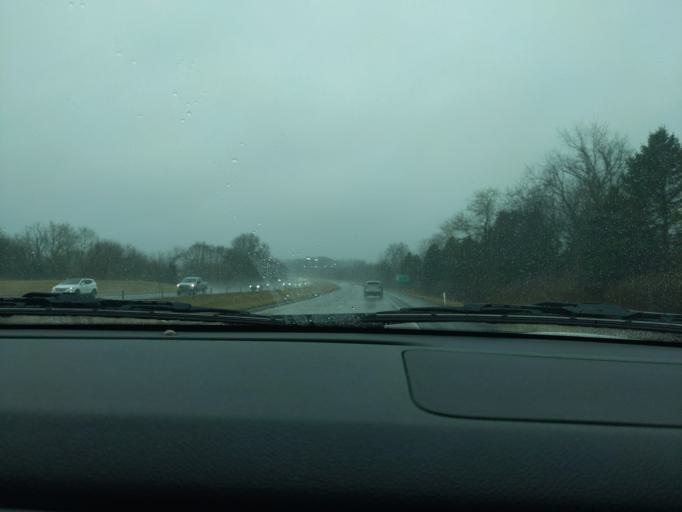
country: US
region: Pennsylvania
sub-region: Bucks County
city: Doylestown
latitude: 40.3116
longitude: -75.1488
